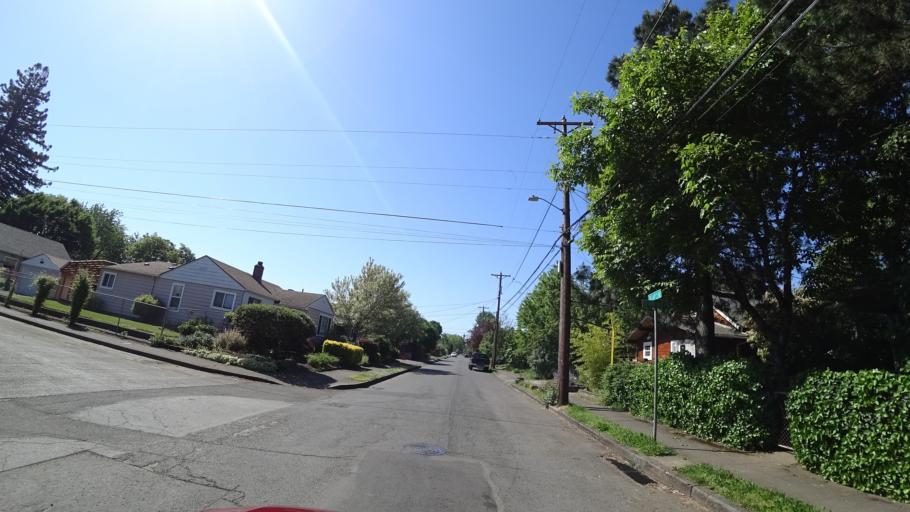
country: US
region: Oregon
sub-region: Multnomah County
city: Lents
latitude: 45.4895
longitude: -122.6013
